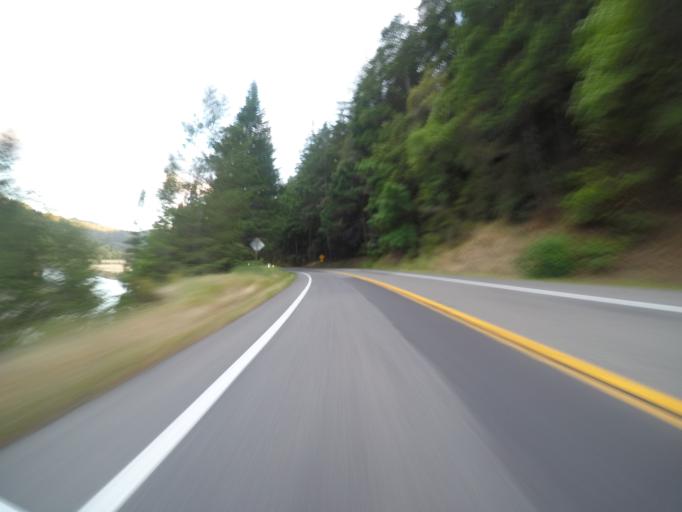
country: US
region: California
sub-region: Humboldt County
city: Redway
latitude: 40.0148
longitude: -123.7916
